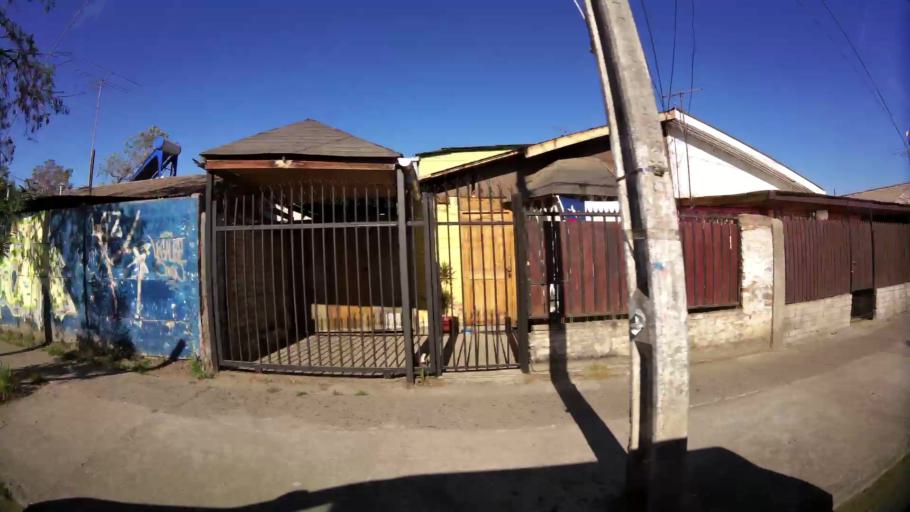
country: CL
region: Santiago Metropolitan
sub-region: Provincia de Talagante
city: Penaflor
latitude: -33.6054
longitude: -70.8681
